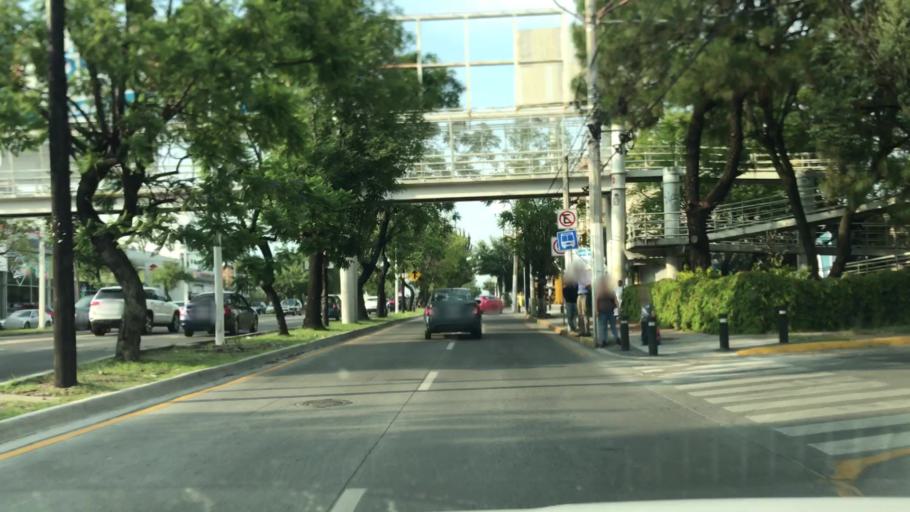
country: MX
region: Jalisco
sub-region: Tlajomulco de Zuniga
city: La Tijera
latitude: 20.6235
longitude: -103.4210
